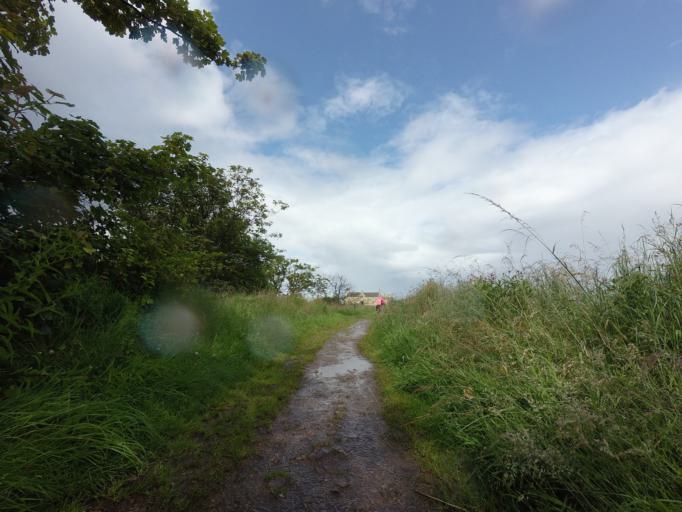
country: GB
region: Scotland
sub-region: Moray
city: Fochabers
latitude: 57.6717
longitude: -3.0924
